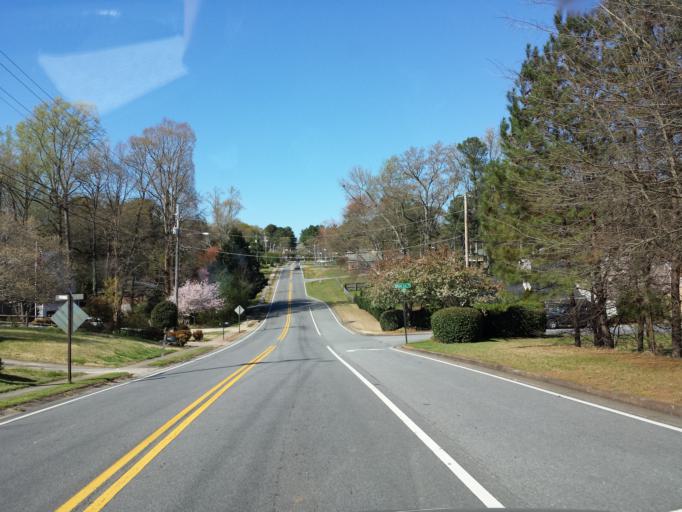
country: US
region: Georgia
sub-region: Cobb County
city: Fair Oaks
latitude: 33.8997
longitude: -84.5533
